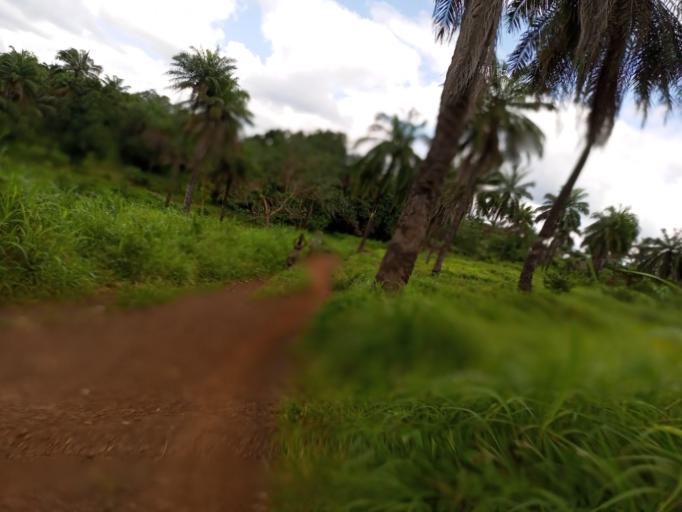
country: SL
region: Northern Province
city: Kamakwie
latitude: 9.4950
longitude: -12.2326
